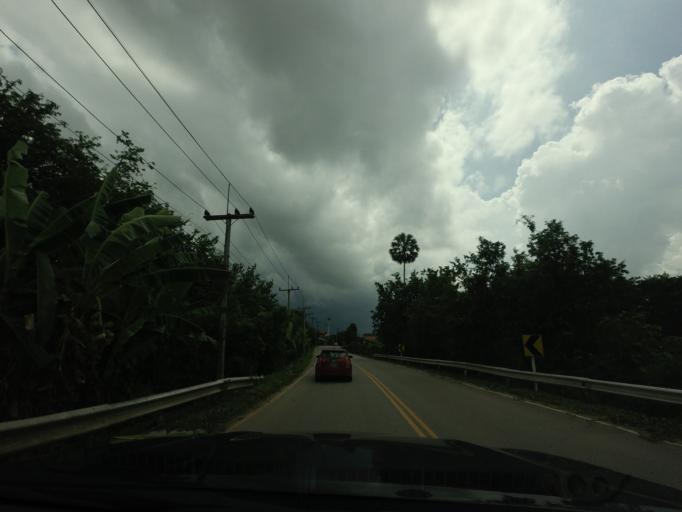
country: LA
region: Vientiane
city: Muang Sanakham
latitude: 18.0057
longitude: 101.7573
